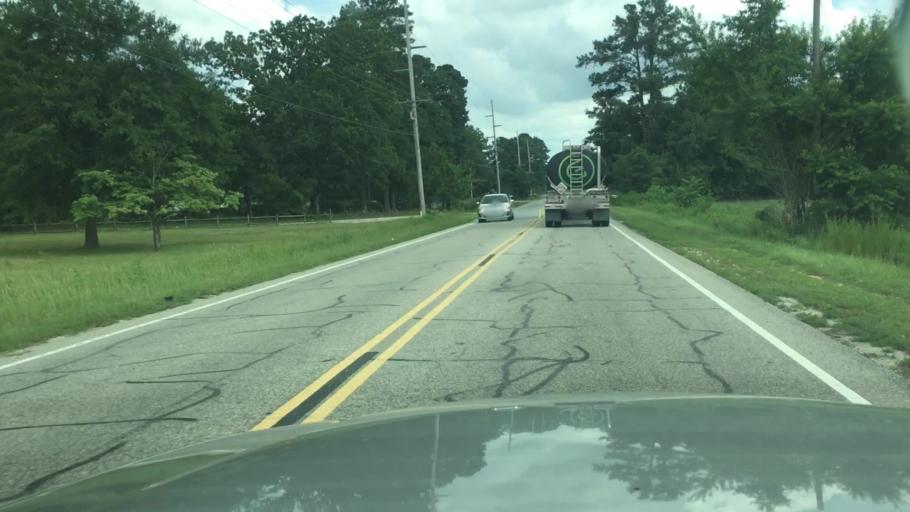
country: US
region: North Carolina
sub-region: Hoke County
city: Rockfish
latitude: 35.0118
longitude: -79.0042
